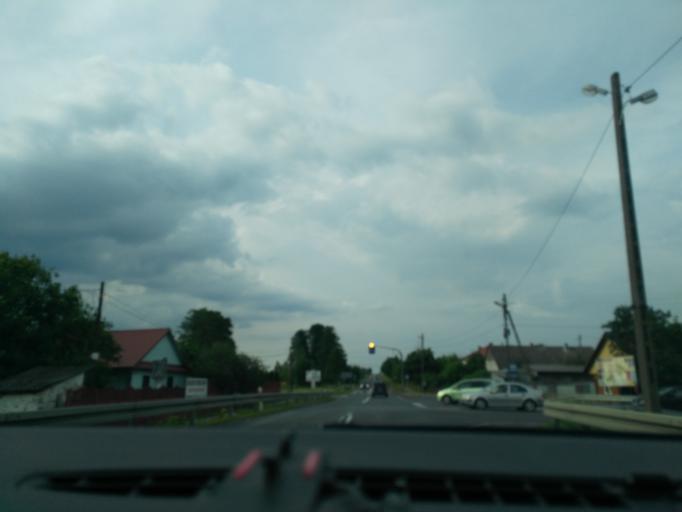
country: PL
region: Subcarpathian Voivodeship
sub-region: Powiat nizanski
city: Jezowe
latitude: 50.3746
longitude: 22.1274
